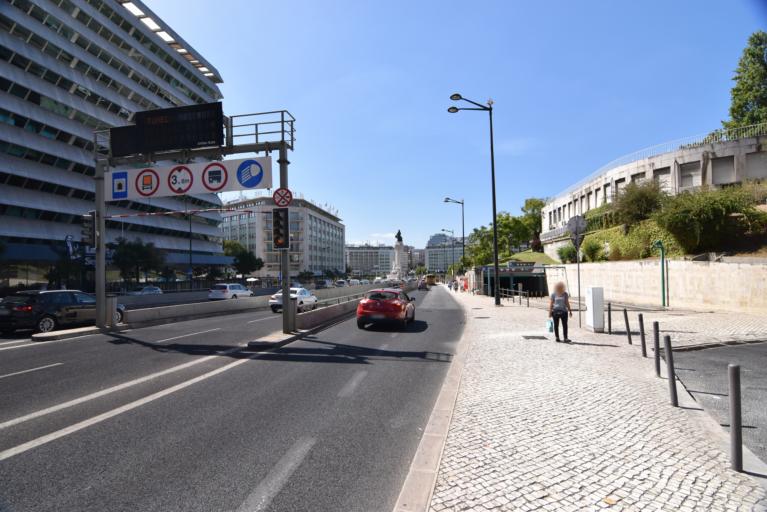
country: PT
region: Lisbon
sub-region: Lisbon
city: Lisbon
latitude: 38.7274
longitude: -9.1491
